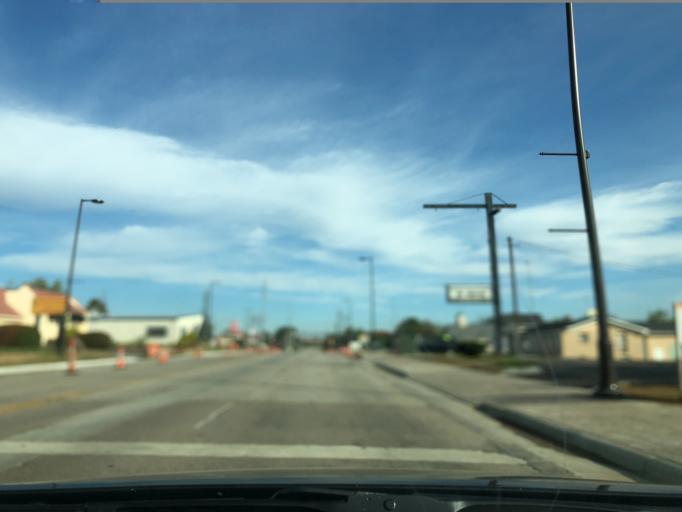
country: US
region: Ohio
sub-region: Hamilton County
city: Glendale
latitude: 39.2827
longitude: -84.4432
